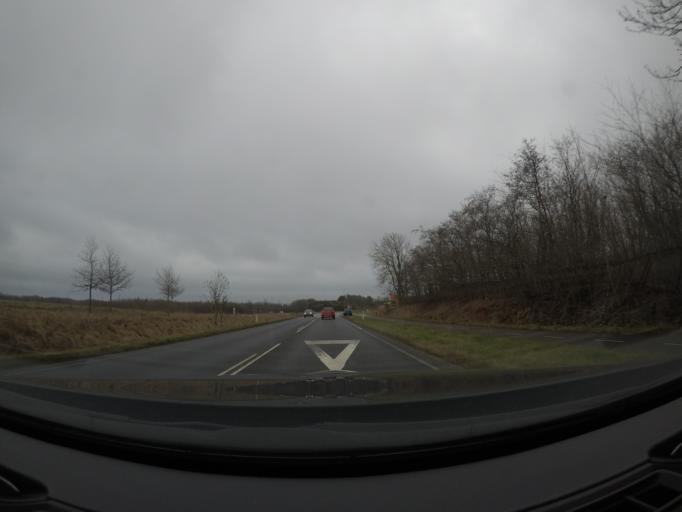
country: DK
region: South Denmark
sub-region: Kolding Kommune
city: Kolding
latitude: 55.5497
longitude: 9.4874
